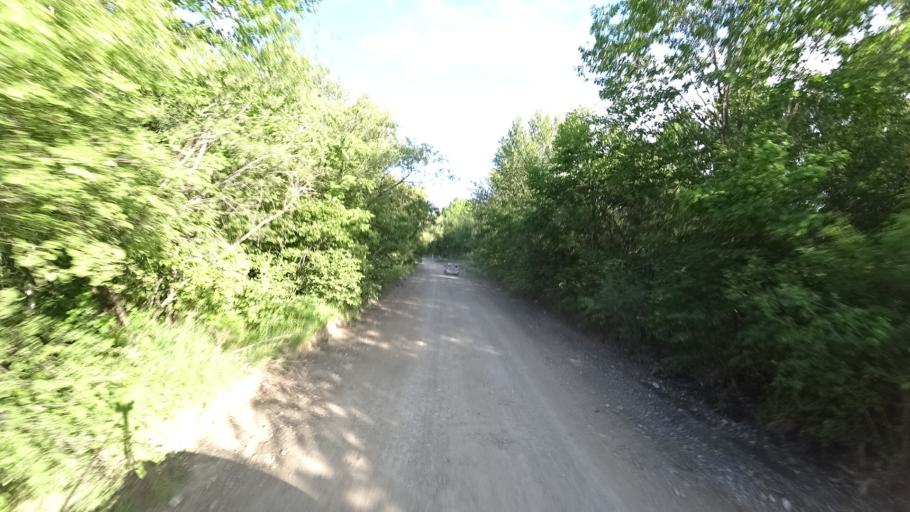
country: RU
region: Khabarovsk Krai
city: Khor
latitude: 47.8513
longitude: 134.9453
